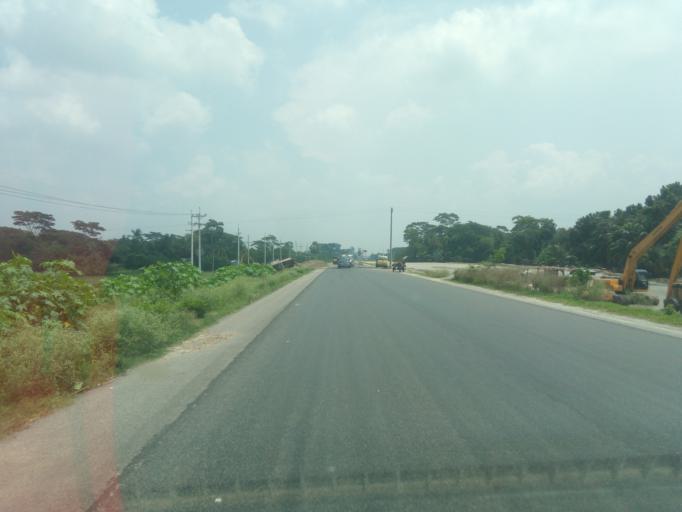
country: BD
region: Dhaka
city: Char Bhadrasan
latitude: 23.3756
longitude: 90.0223
